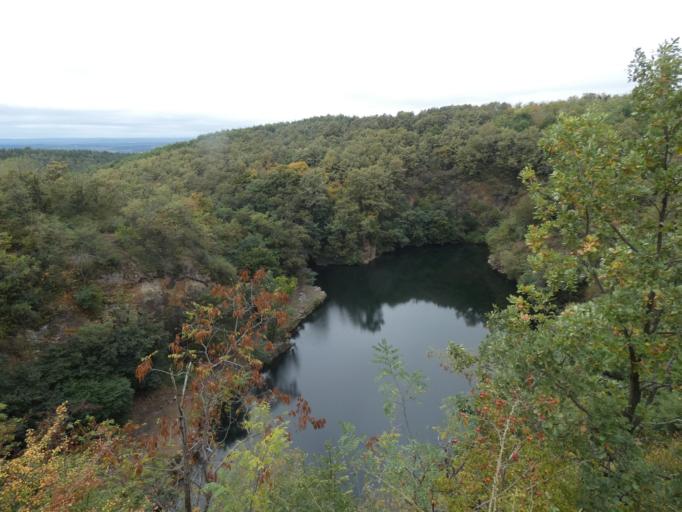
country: HU
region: Heves
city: Apc
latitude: 47.8125
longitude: 19.7150
